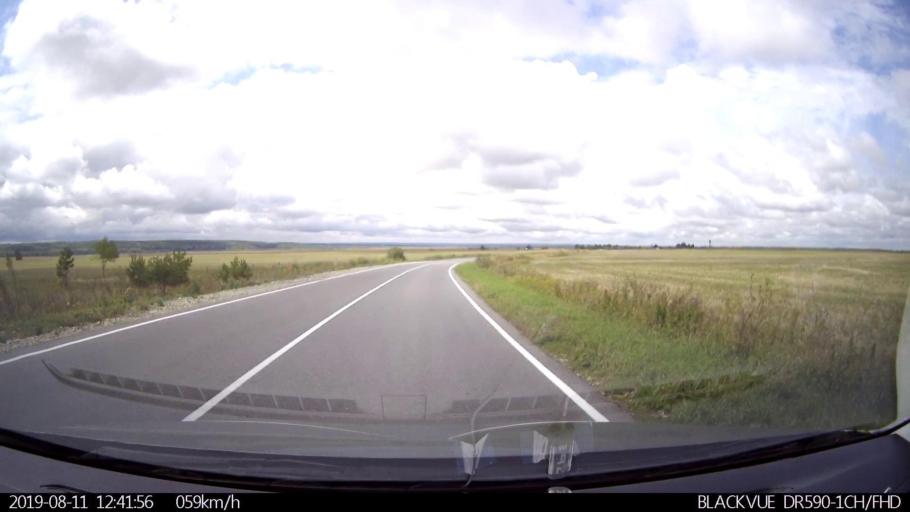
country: RU
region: Ulyanovsk
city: Ignatovka
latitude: 53.8425
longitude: 47.7577
